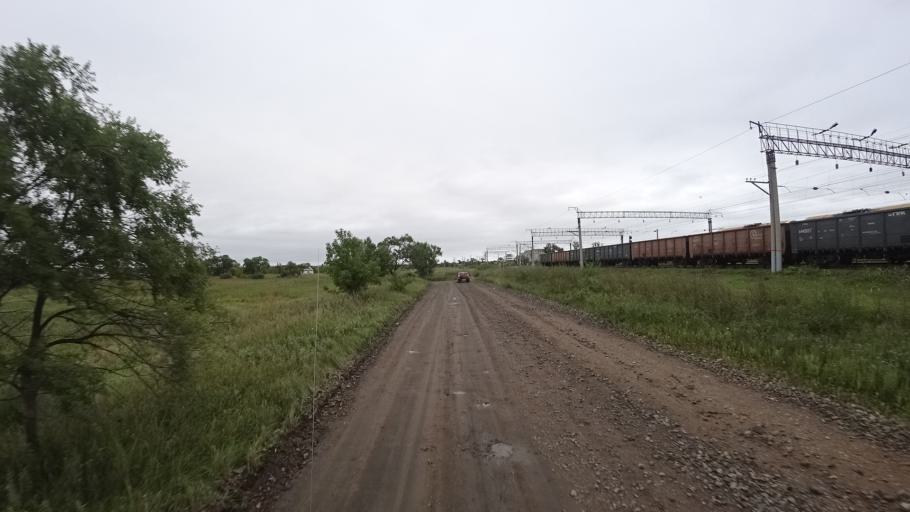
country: RU
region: Primorskiy
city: Chernigovka
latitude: 44.3418
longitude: 132.5353
